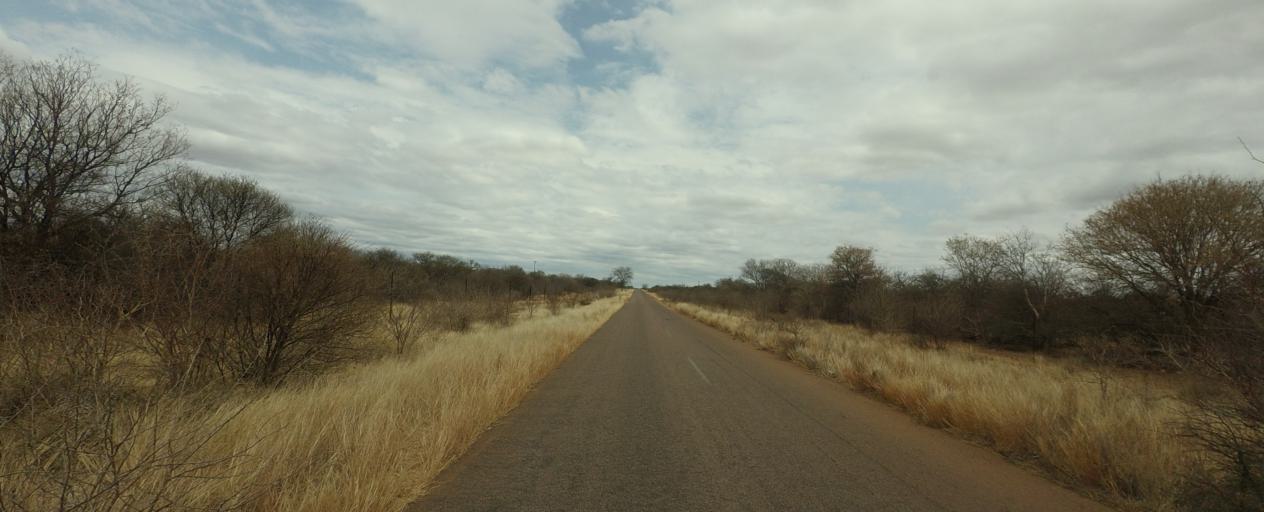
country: BW
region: Central
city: Mathathane
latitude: -22.6635
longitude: 28.7015
